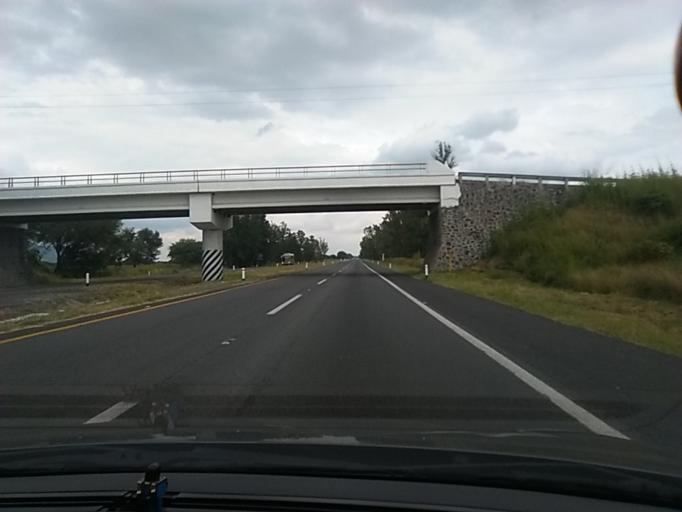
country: MX
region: Jalisco
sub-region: Ocotlan
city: Joconoxtle (La Tuna)
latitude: 20.3796
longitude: -102.6914
